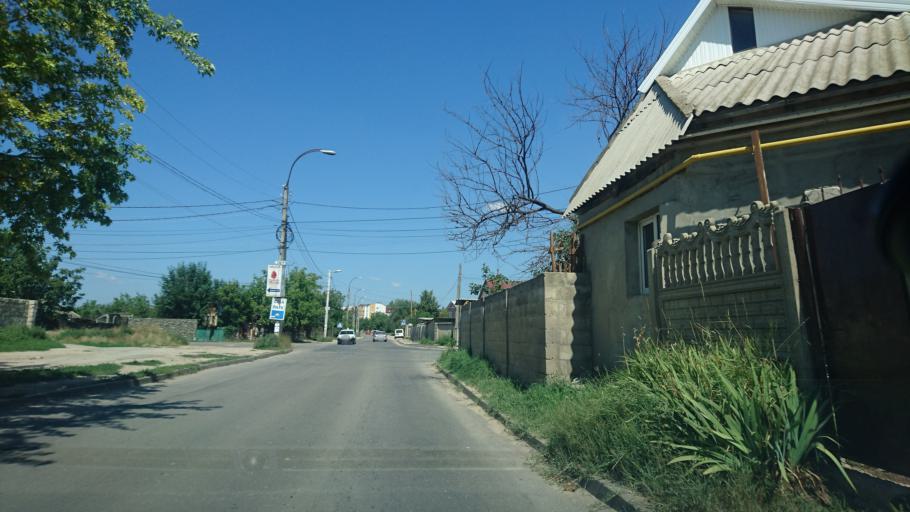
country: MD
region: Laloveni
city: Ialoveni
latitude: 46.9969
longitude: 28.7844
